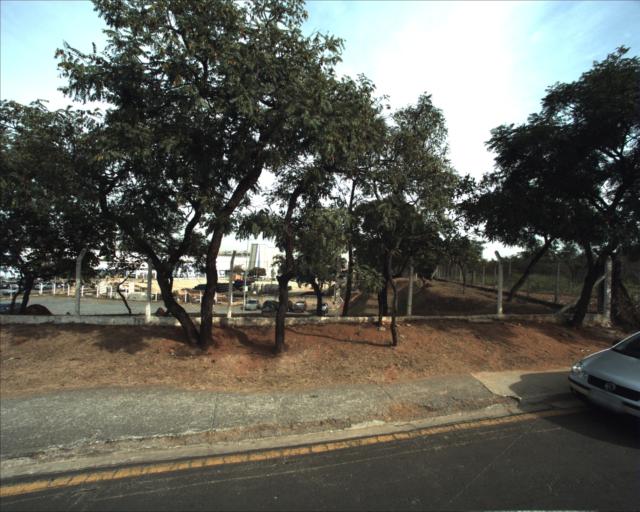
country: BR
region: Sao Paulo
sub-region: Sorocaba
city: Sorocaba
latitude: -23.4643
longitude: -47.4524
